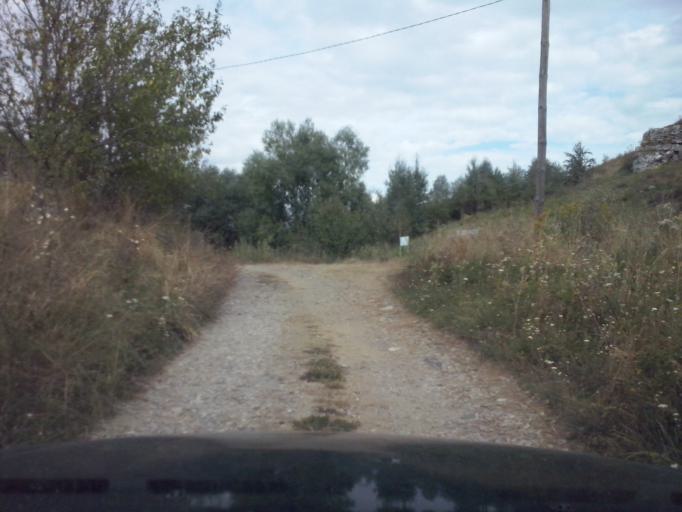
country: PL
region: Swietokrzyskie
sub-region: Powiat kielecki
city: Lagow
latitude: 50.7825
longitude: 21.0913
